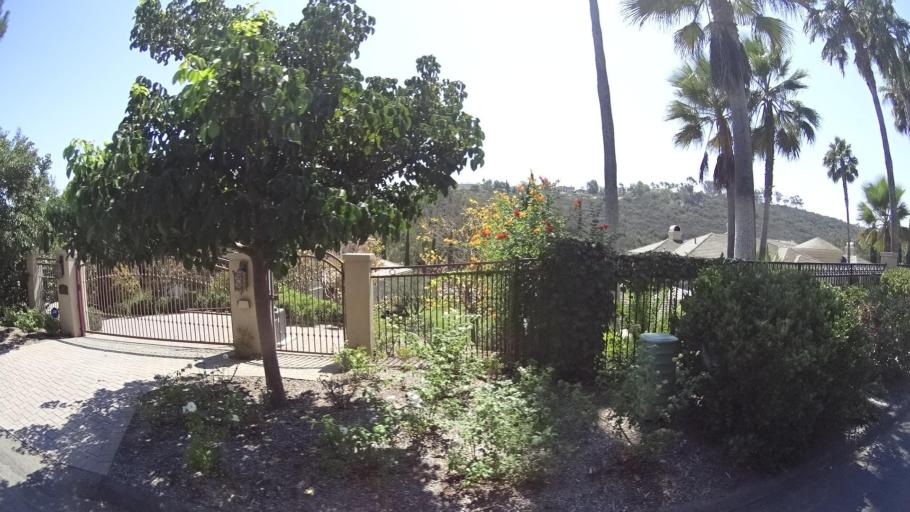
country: US
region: California
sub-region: San Diego County
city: Fairbanks Ranch
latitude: 32.9793
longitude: -117.1725
